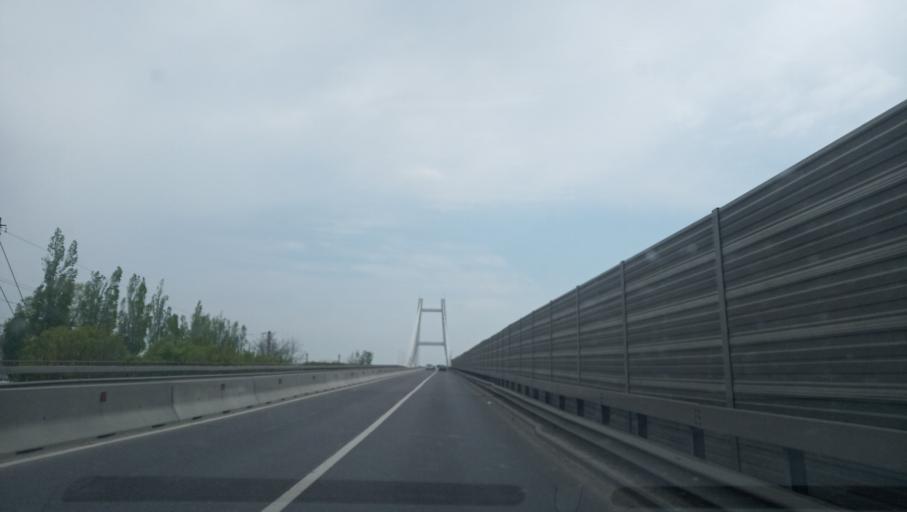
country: RO
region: Ilfov
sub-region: Comuna Otopeni
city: Otopeni
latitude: 44.5355
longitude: 26.0726
